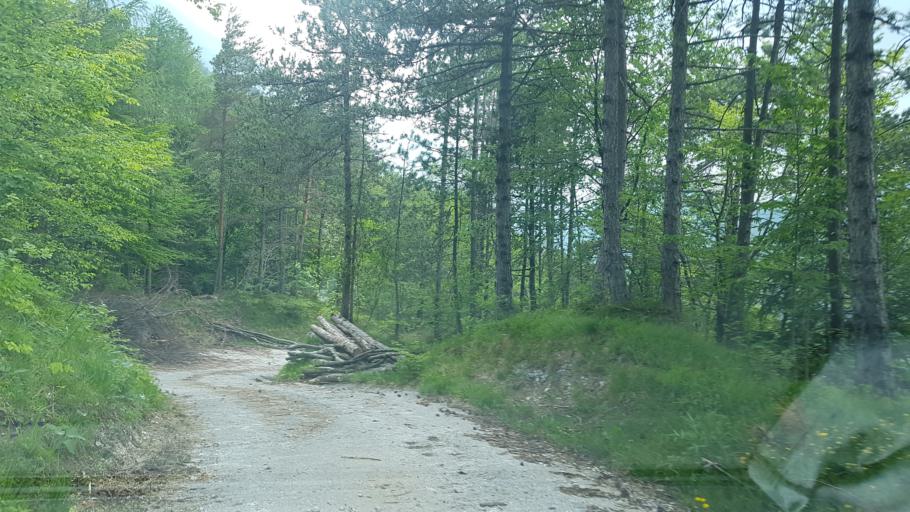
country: IT
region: Friuli Venezia Giulia
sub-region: Provincia di Udine
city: Cavazzo Carnico
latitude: 46.3514
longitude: 13.0249
